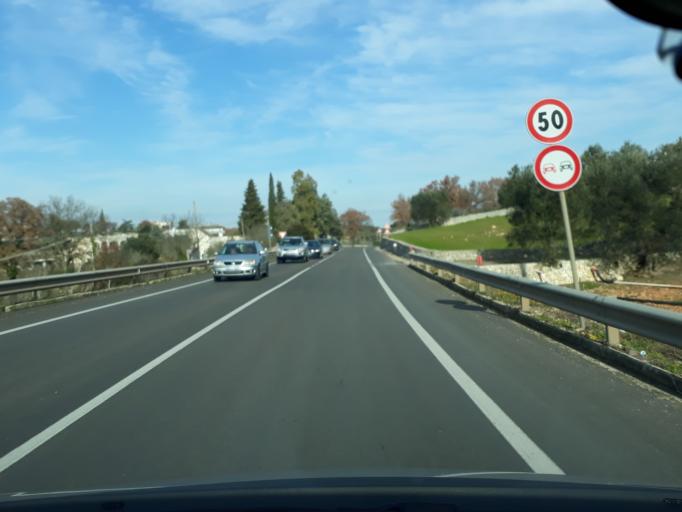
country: IT
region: Apulia
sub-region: Provincia di Bari
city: Locorotondo
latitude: 40.7839
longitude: 17.3397
